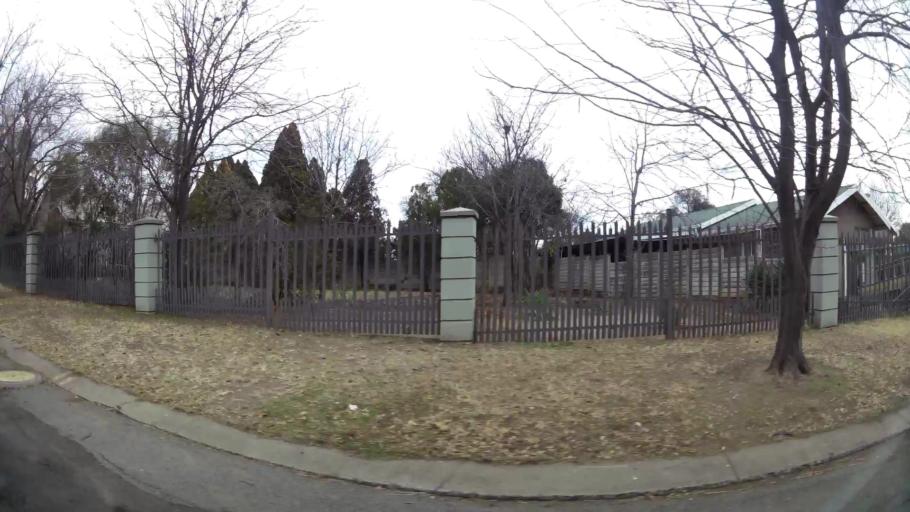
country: ZA
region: Orange Free State
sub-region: Fezile Dabi District Municipality
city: Kroonstad
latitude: -27.6823
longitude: 27.2406
